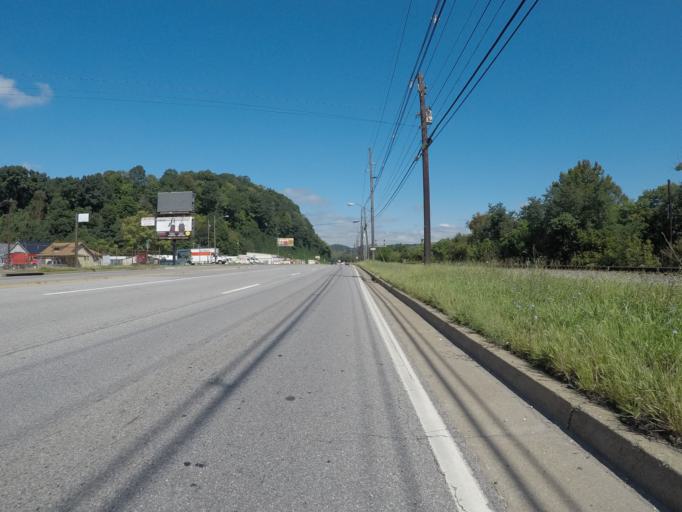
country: US
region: Kentucky
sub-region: Boyd County
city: Ashland
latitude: 38.4549
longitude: -82.6126
